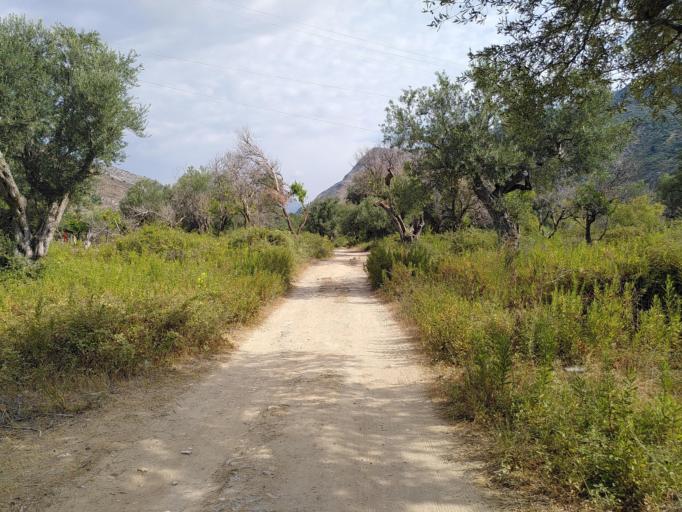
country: AL
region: Vlore
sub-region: Rrethi i Vlores
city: Himare
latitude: 40.0553
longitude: 19.8195
